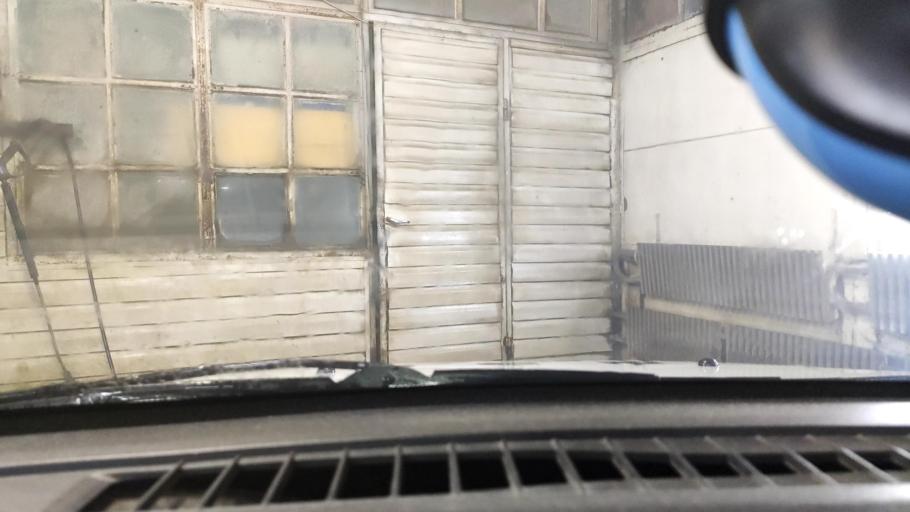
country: RU
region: Perm
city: Kondratovo
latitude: 58.0329
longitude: 56.0381
